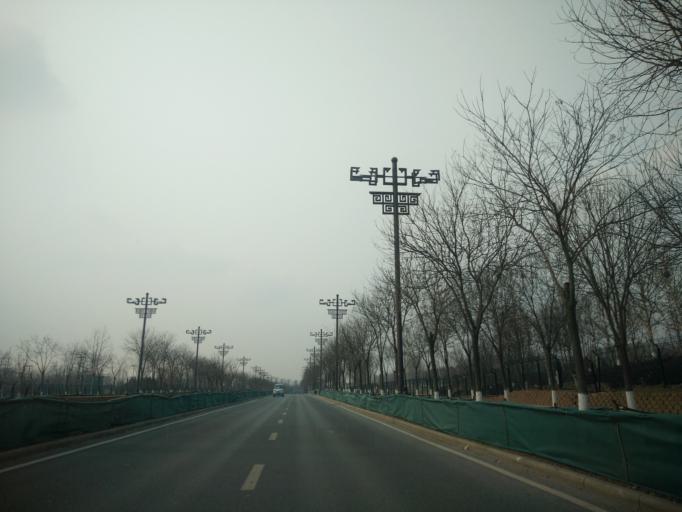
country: CN
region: Beijing
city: Yinghai
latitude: 39.7673
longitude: 116.4626
